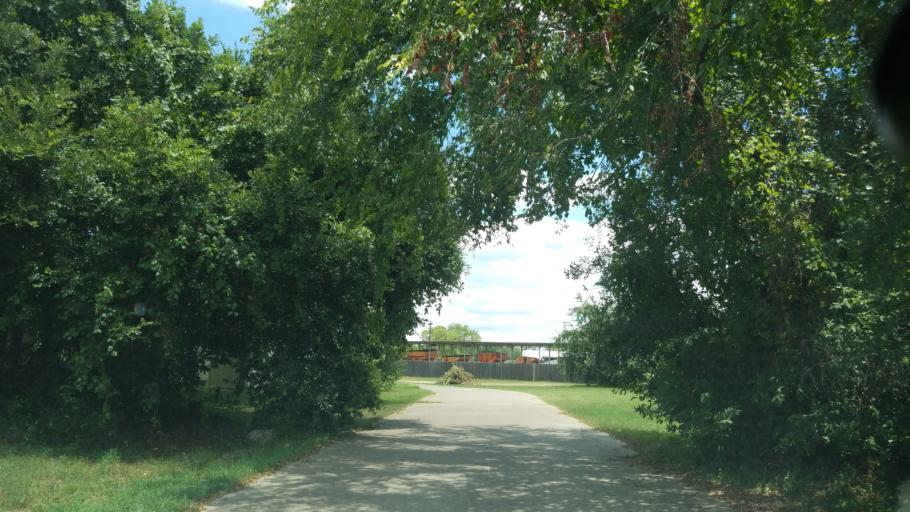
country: US
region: Texas
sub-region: Dallas County
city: Dallas
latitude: 32.7352
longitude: -96.7516
